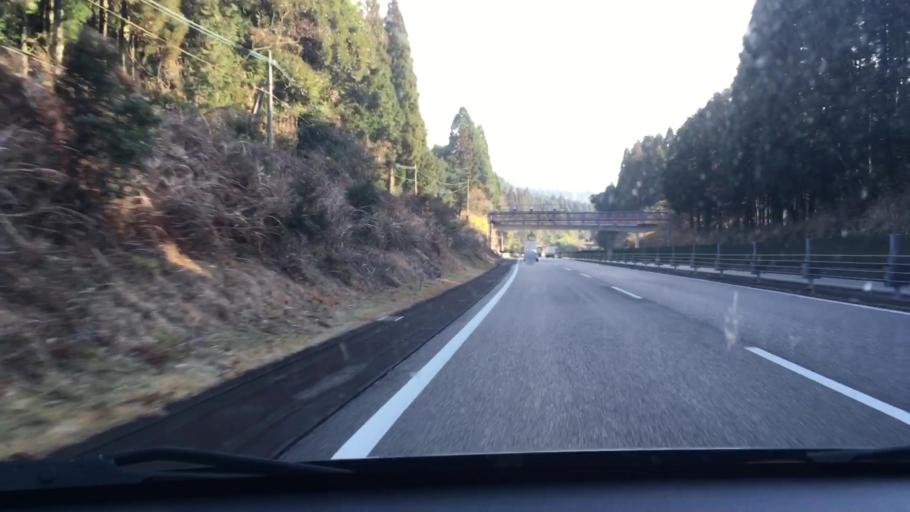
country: JP
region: Kagoshima
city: Okuchi-shinohara
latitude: 32.0026
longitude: 130.7568
